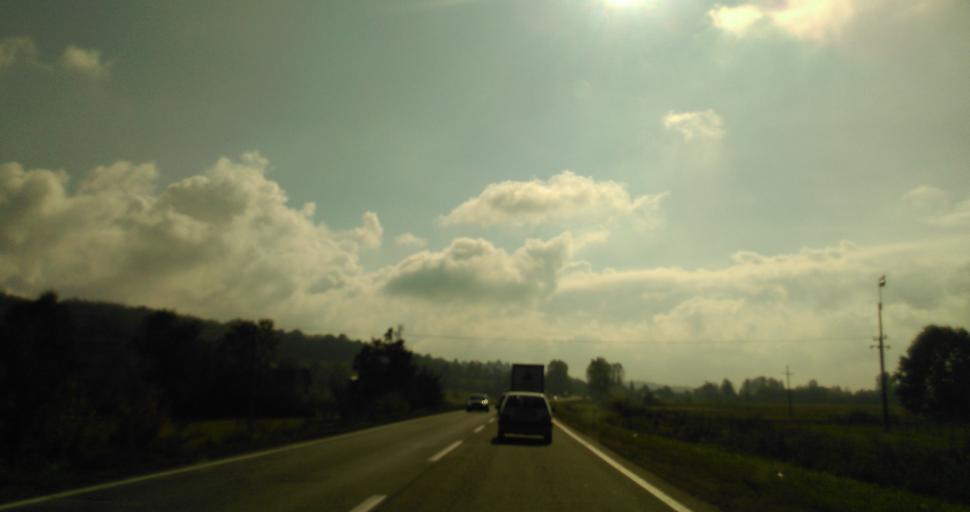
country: RS
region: Central Serbia
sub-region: Kolubarski Okrug
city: Lajkovac
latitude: 44.3416
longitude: 20.2053
